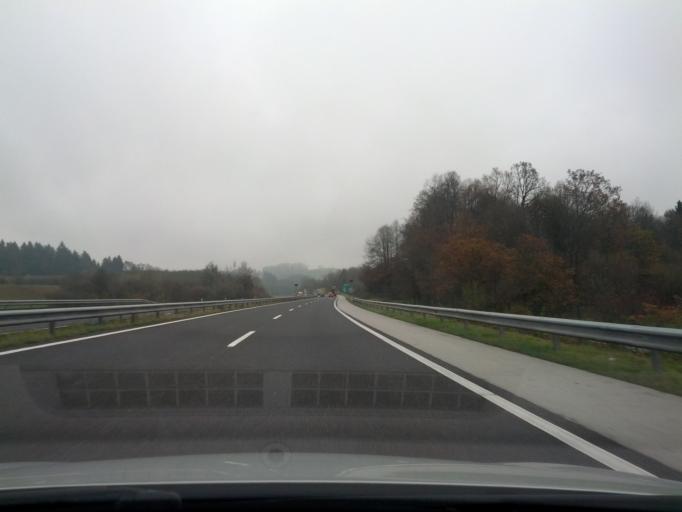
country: SI
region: Ivancna Gorica
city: Sentvid pri Sticni
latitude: 45.9330
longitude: 14.8429
